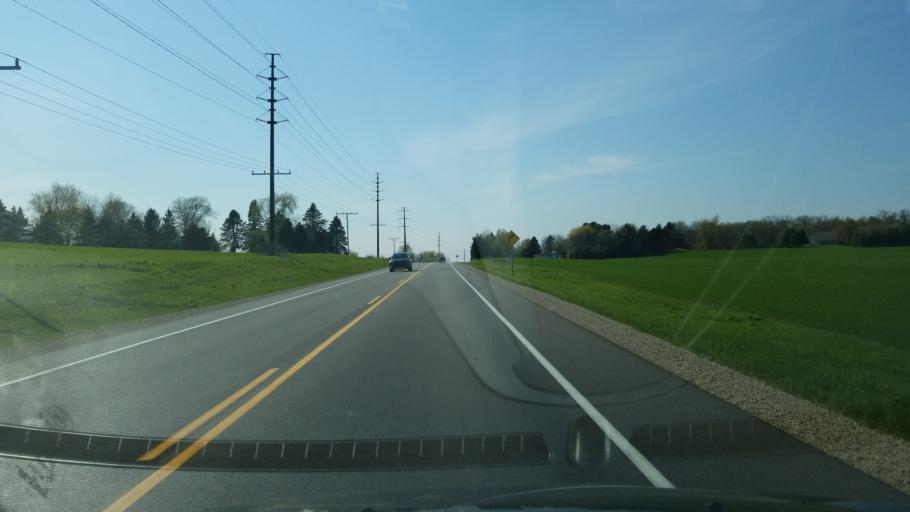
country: US
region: Wisconsin
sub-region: Dane County
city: Fitchburg
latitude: 42.9655
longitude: -89.4900
